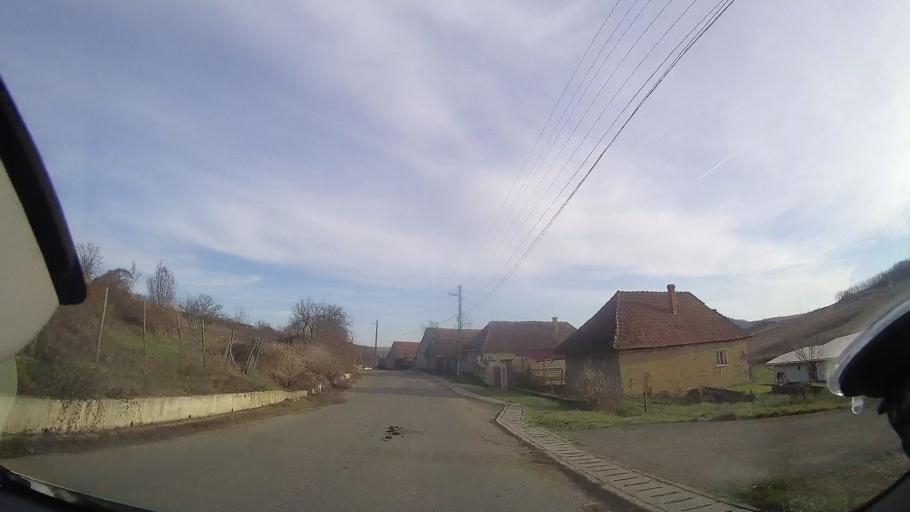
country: RO
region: Bihor
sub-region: Comuna Sarbi
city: Burzuc
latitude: 47.1485
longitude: 22.1760
